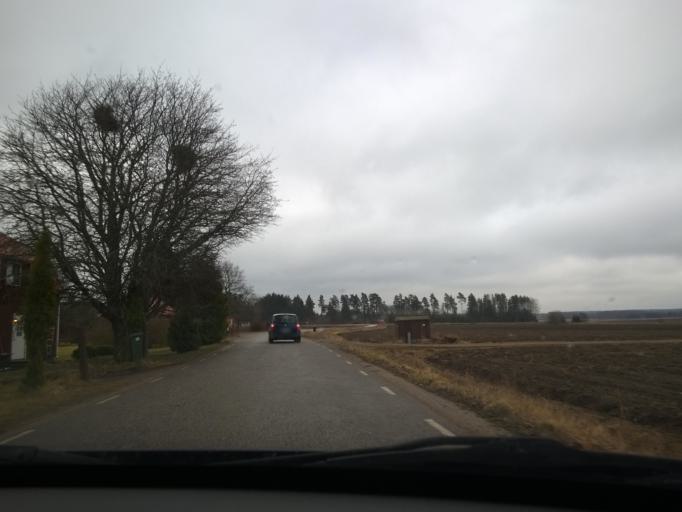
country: SE
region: Uppsala
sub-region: Osthammars Kommun
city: Bjorklinge
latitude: 60.1620
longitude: 17.5274
